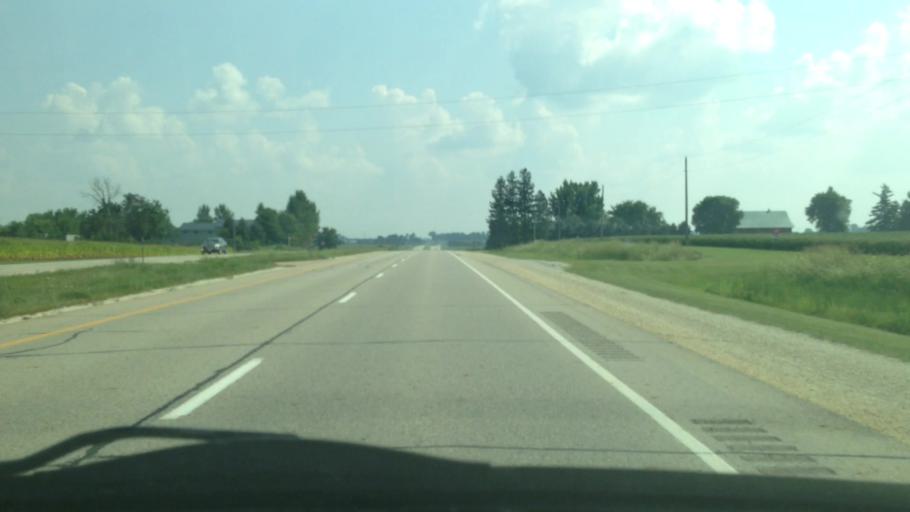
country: US
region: Iowa
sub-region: Bremer County
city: Denver
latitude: 42.6311
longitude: -92.3377
